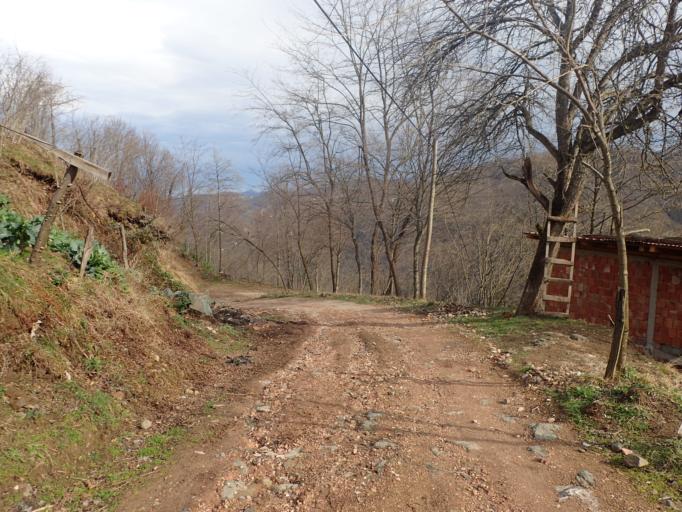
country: TR
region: Ordu
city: Camas
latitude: 40.8852
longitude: 37.5809
